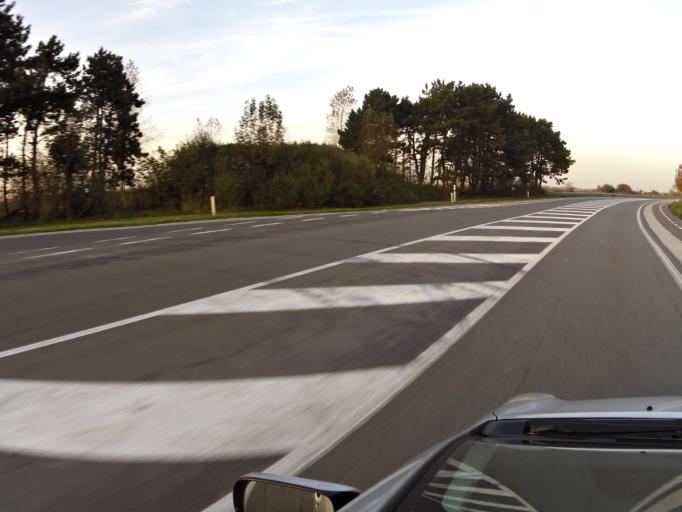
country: BE
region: Flanders
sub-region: Provincie West-Vlaanderen
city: Veurne
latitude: 51.1063
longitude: 2.7050
